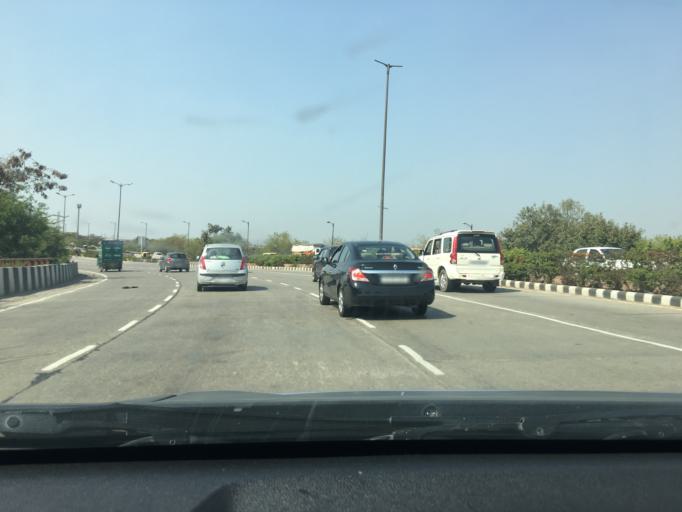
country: IN
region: NCT
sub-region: North Delhi
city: Delhi
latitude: 28.6581
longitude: 77.2483
